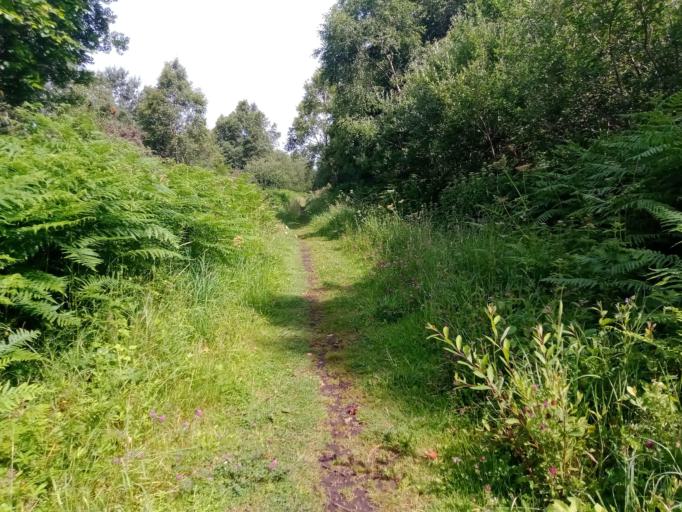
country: IE
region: Leinster
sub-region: Laois
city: Abbeyleix
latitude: 52.8920
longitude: -7.3502
